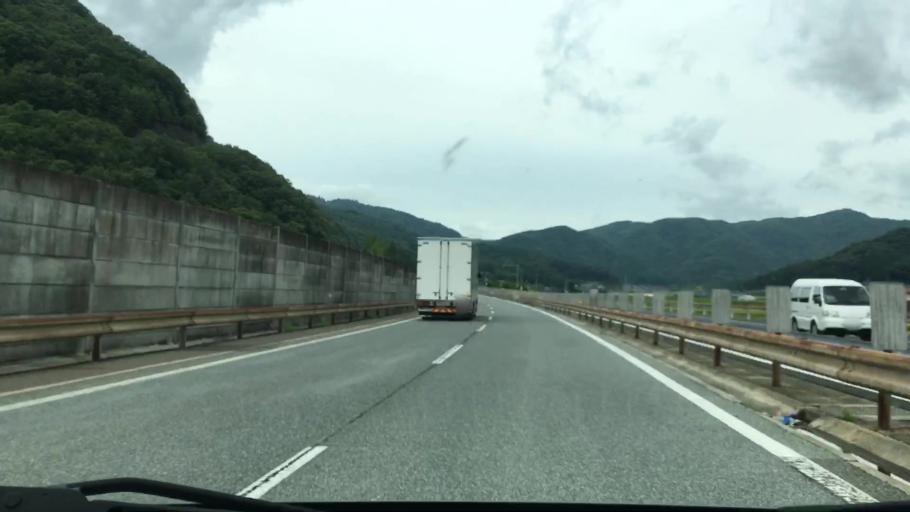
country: JP
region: Okayama
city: Niimi
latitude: 34.9693
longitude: 133.6271
